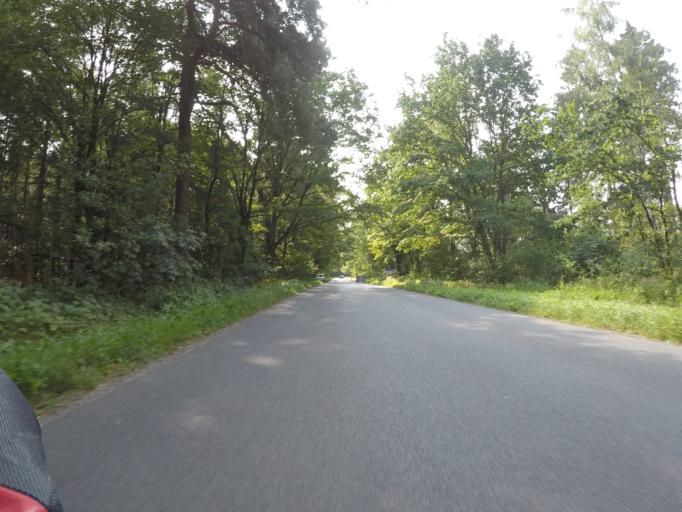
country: DE
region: Schleswig-Holstein
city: Tangstedt
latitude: 53.7158
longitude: 10.0597
